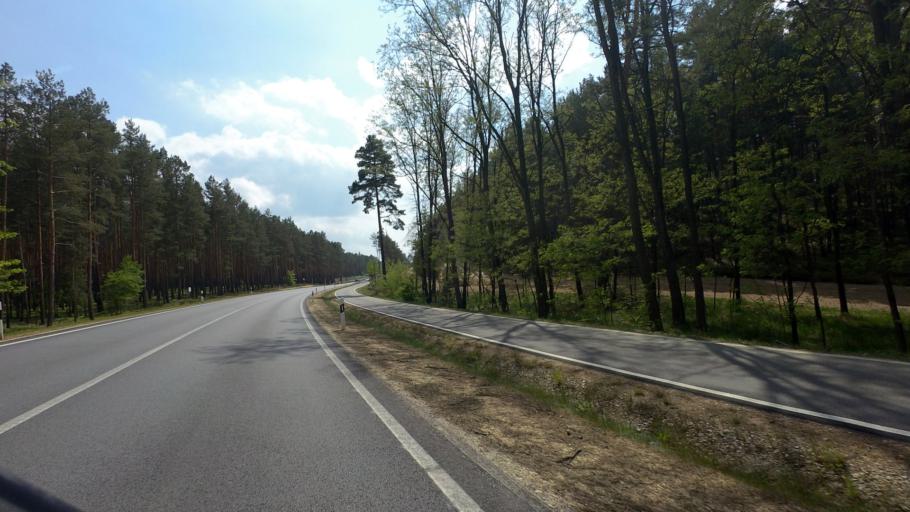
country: DE
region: Saxony
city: Rietschen
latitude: 51.4224
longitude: 14.7895
